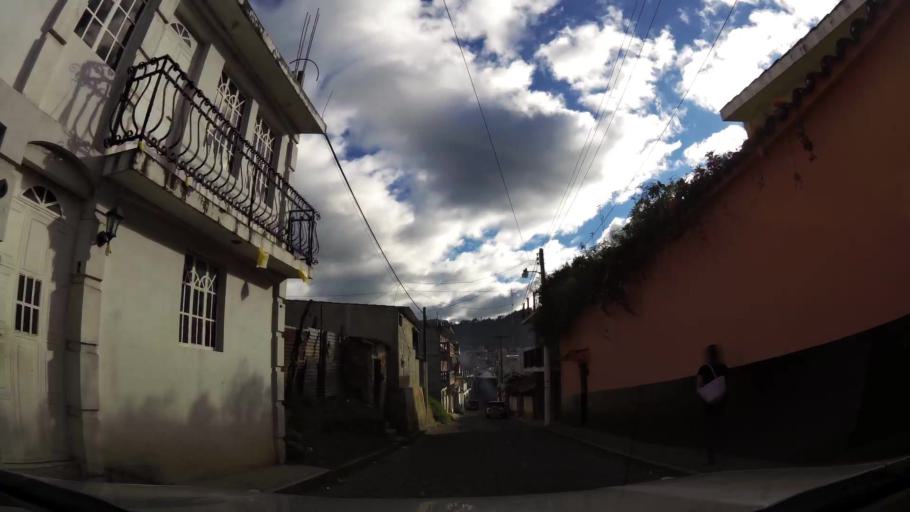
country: GT
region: Quiche
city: Chichicastenango
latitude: 14.9459
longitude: -91.1118
